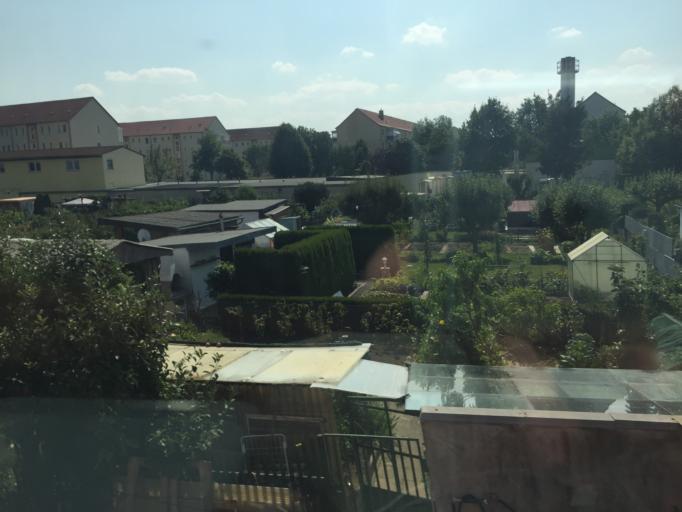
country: DE
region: Saxony
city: Grossenhain
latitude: 51.2991
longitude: 13.5306
